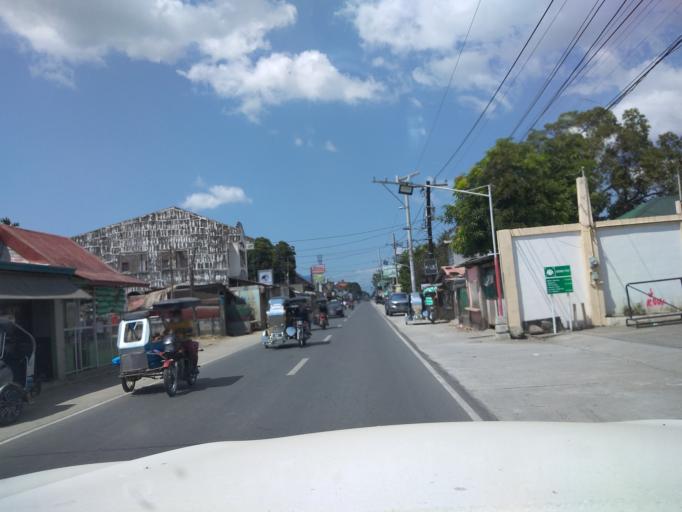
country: PH
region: Central Luzon
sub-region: Province of Pampanga
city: Bahay Pare
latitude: 15.0281
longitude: 120.8823
